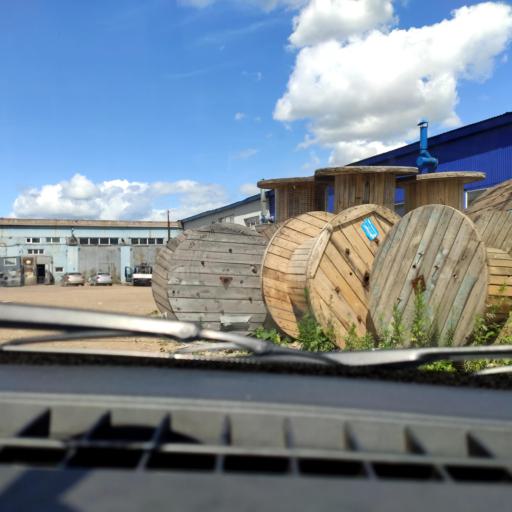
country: RU
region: Bashkortostan
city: Ufa
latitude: 54.8384
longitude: 56.1136
